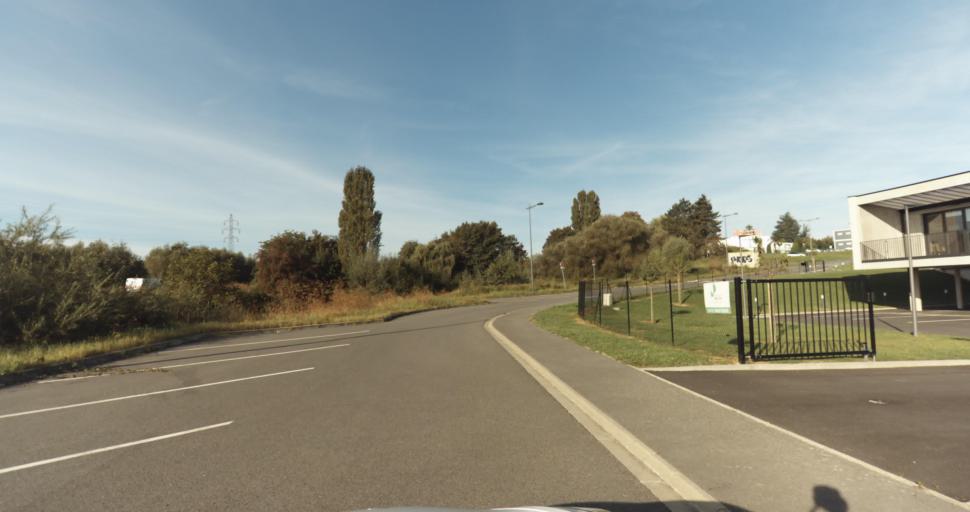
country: FR
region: Champagne-Ardenne
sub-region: Departement des Ardennes
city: Villers-Semeuse
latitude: 49.7361
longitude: 4.7476
